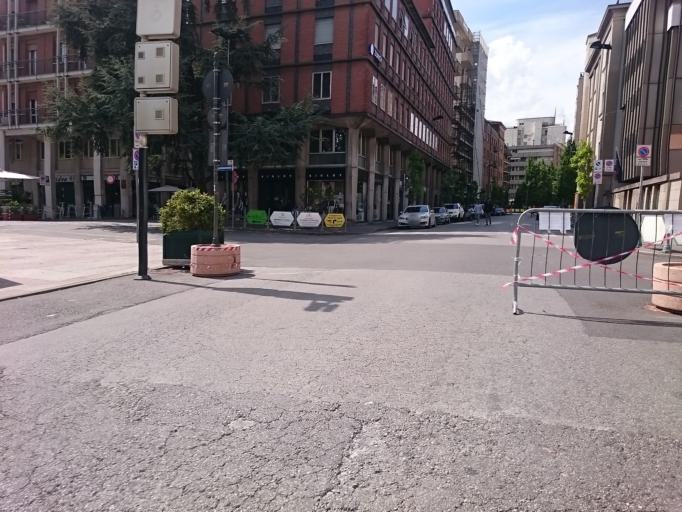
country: IT
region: Veneto
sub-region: Provincia di Rovigo
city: Rovigo
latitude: 45.0710
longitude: 11.7875
